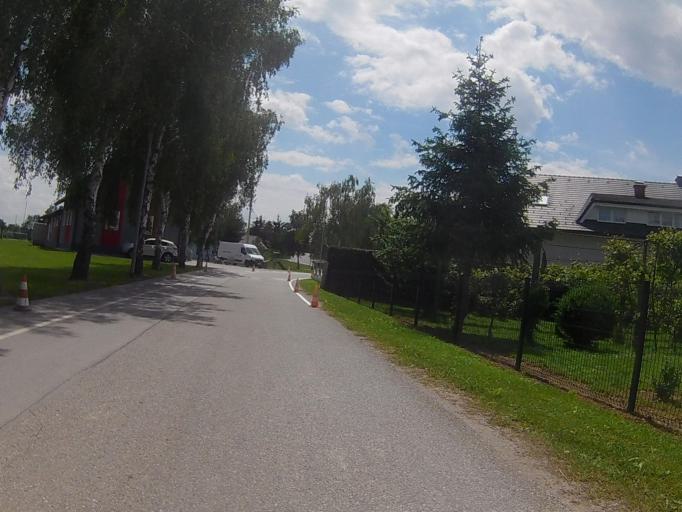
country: SI
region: Kidricevo
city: Kidricevo
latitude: 46.4423
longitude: 15.8124
